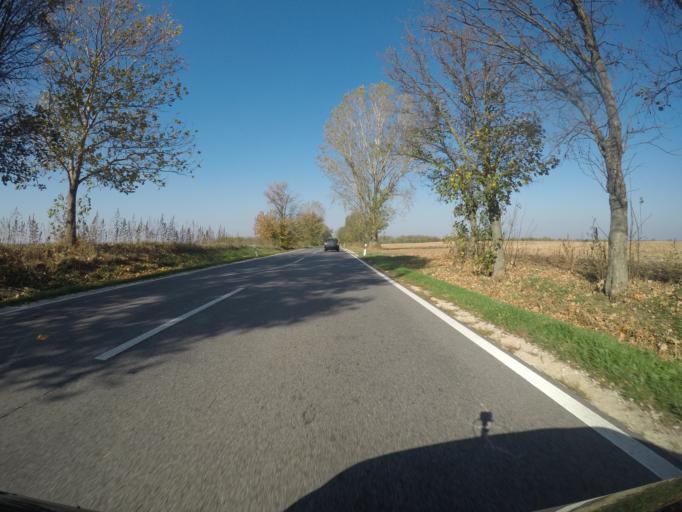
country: HU
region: Tolna
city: Tengelic
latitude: 46.5532
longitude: 18.6510
